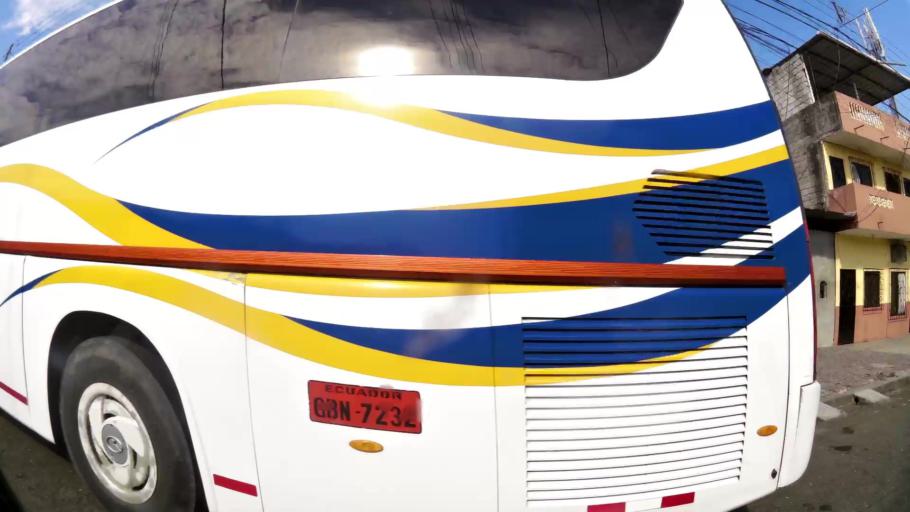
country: EC
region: Guayas
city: Guayaquil
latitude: -2.2192
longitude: -79.9056
